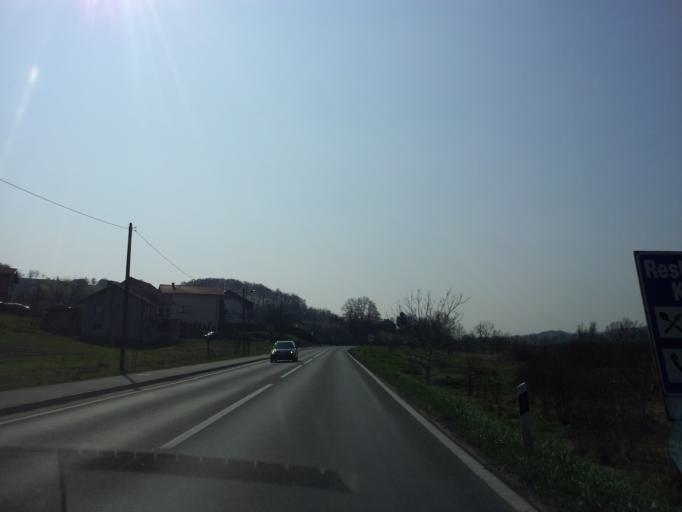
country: HR
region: Karlovacka
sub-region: Grad Karlovac
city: Karlovac
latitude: 45.4221
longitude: 15.6067
